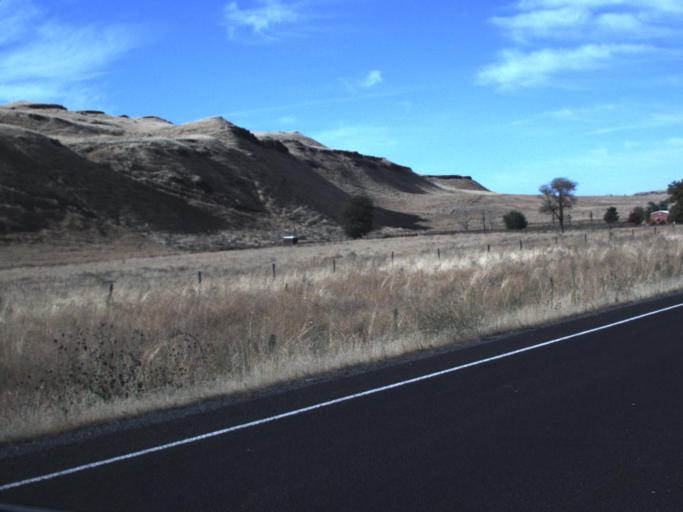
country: US
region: Washington
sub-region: Franklin County
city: Connell
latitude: 46.6473
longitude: -118.5859
